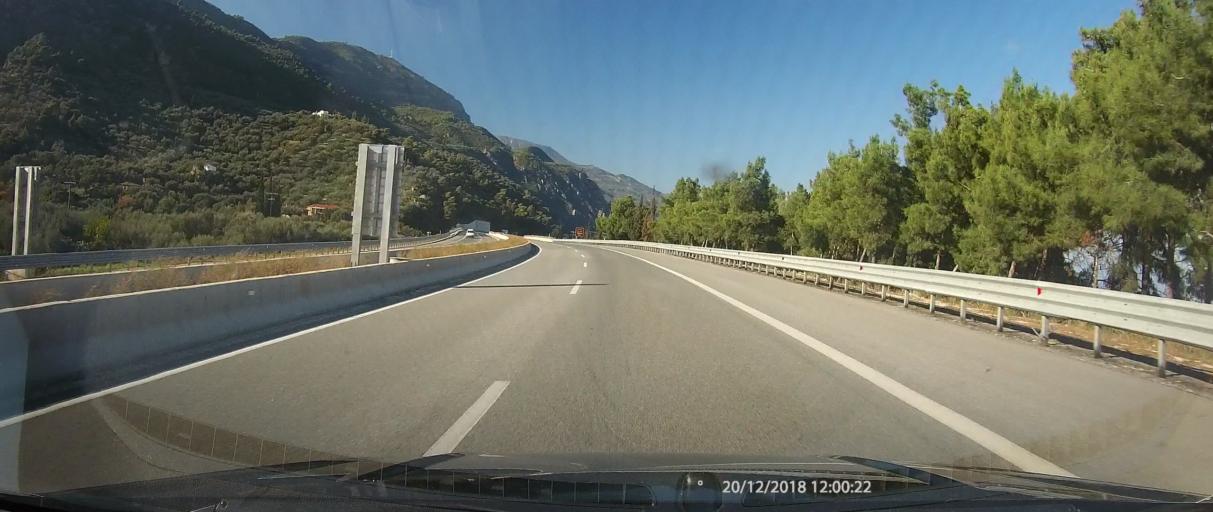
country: GR
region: West Greece
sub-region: Nomos Achaias
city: Temeni
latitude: 38.1843
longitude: 22.1950
